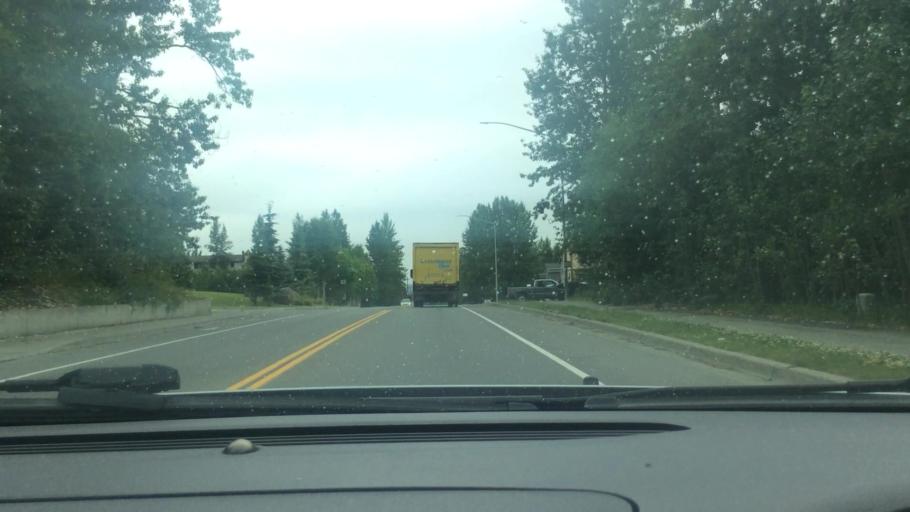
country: US
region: Alaska
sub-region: Anchorage Municipality
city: Elmendorf Air Force Base
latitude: 61.2192
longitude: -149.7561
